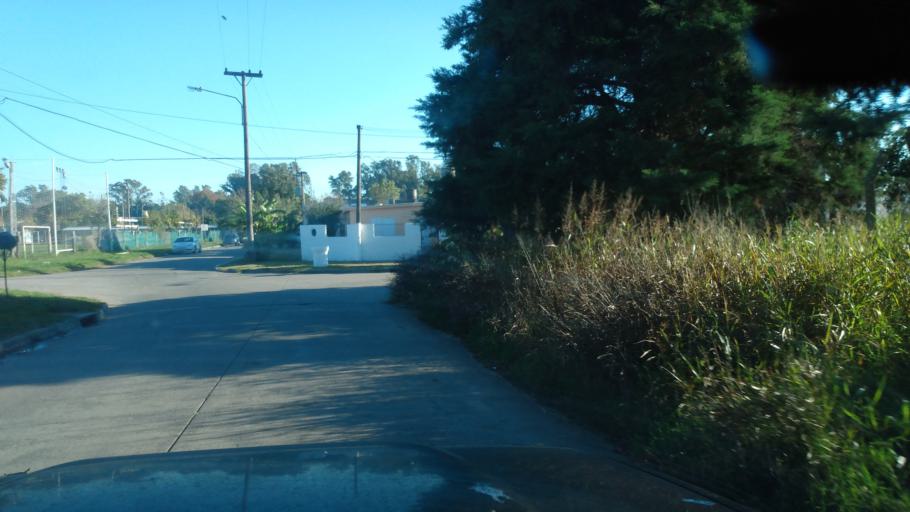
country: AR
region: Buenos Aires
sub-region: Partido de Lujan
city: Lujan
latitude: -34.5617
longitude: -59.0964
